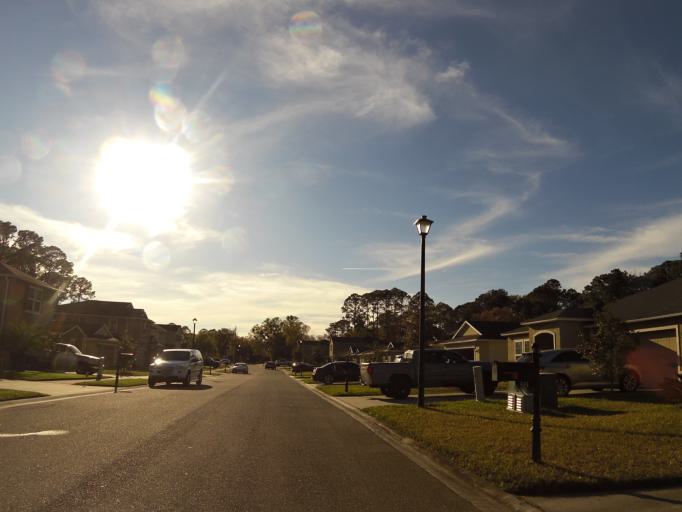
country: US
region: Florida
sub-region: Duval County
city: Jacksonville
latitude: 30.4631
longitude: -81.6242
